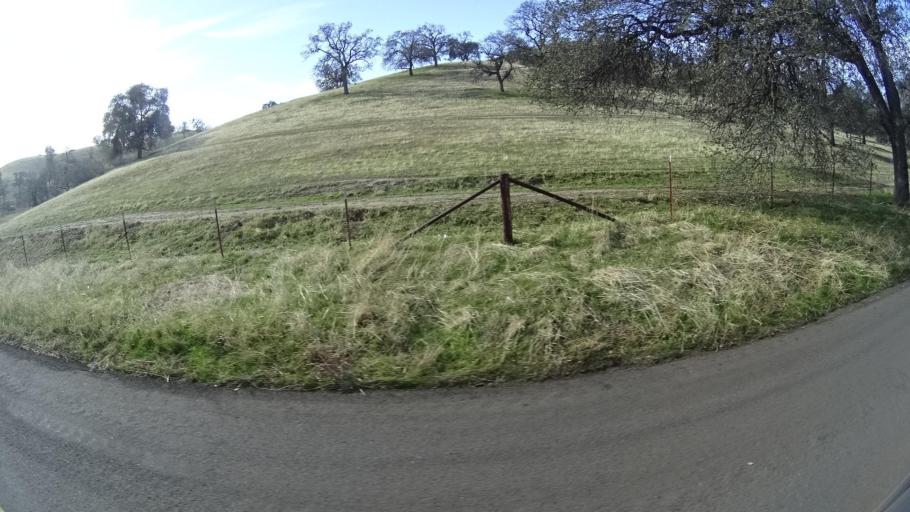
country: US
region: California
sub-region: Tulare County
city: Richgrove
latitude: 35.6670
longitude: -118.8480
